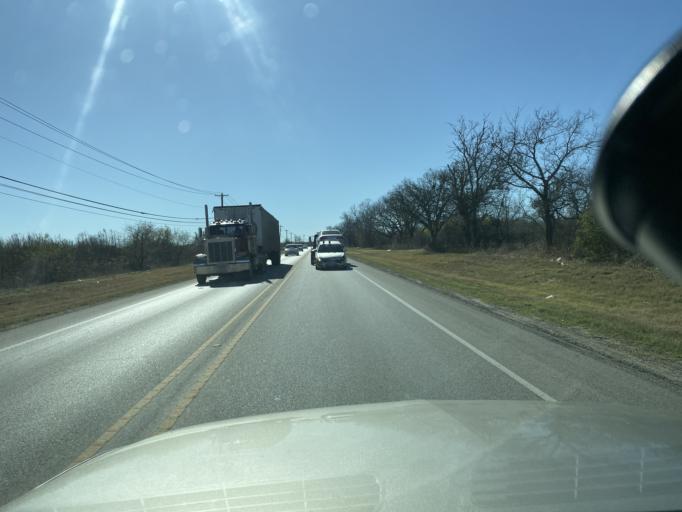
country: US
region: Texas
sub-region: Travis County
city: Garfield
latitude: 30.1769
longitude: -97.6486
